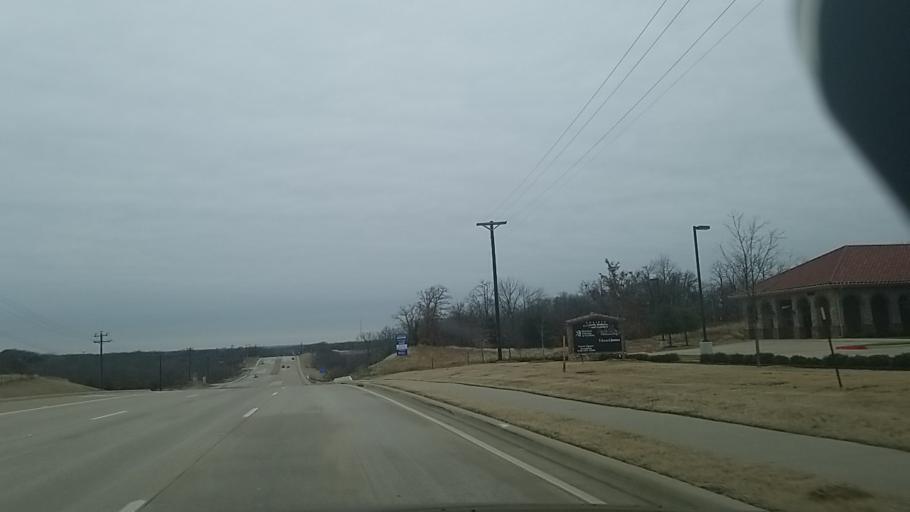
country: US
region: Texas
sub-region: Denton County
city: Hickory Creek
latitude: 33.1303
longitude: -97.0639
